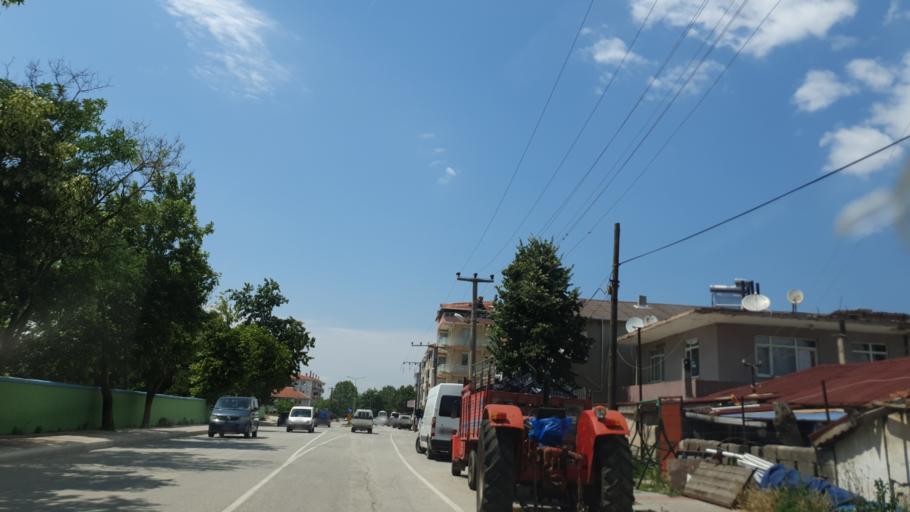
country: TR
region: Tekirdag
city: Saray
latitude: 41.4400
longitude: 27.9148
